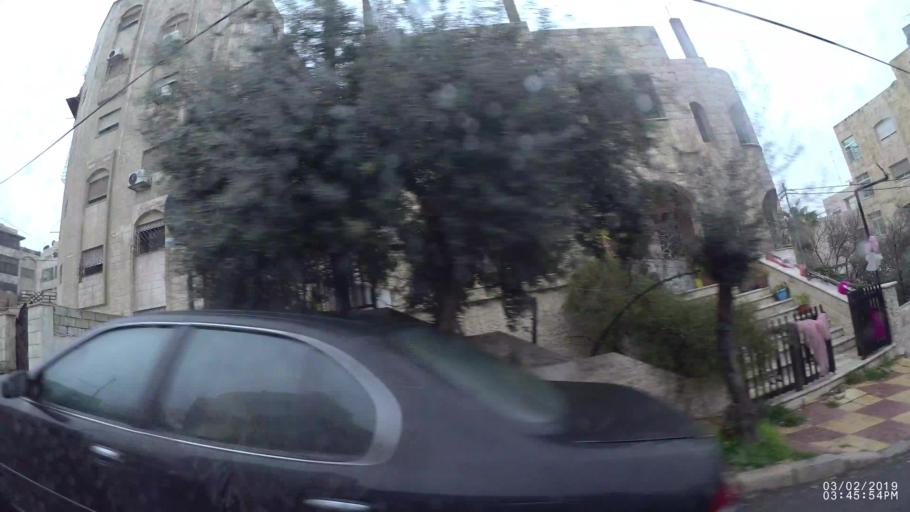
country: JO
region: Amman
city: Amman
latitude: 31.9759
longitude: 35.9183
